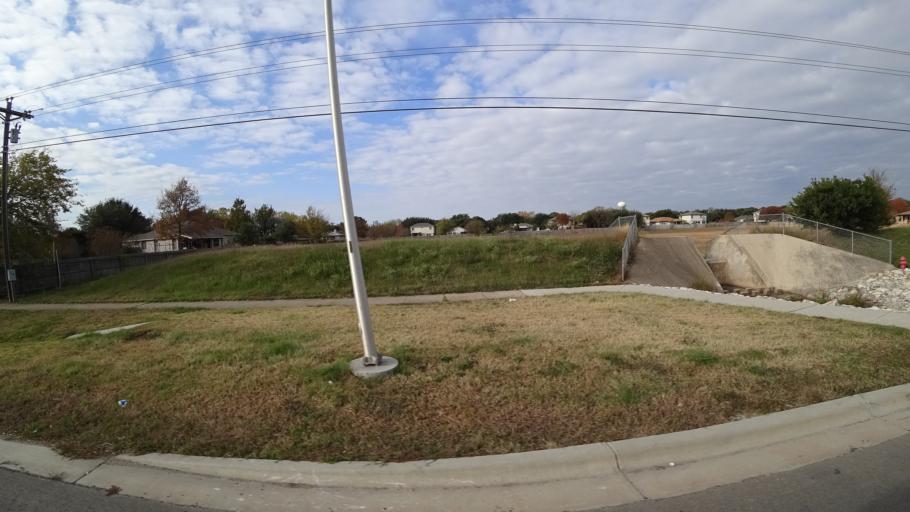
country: US
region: Texas
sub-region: Williamson County
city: Cedar Park
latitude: 30.5216
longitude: -97.8418
